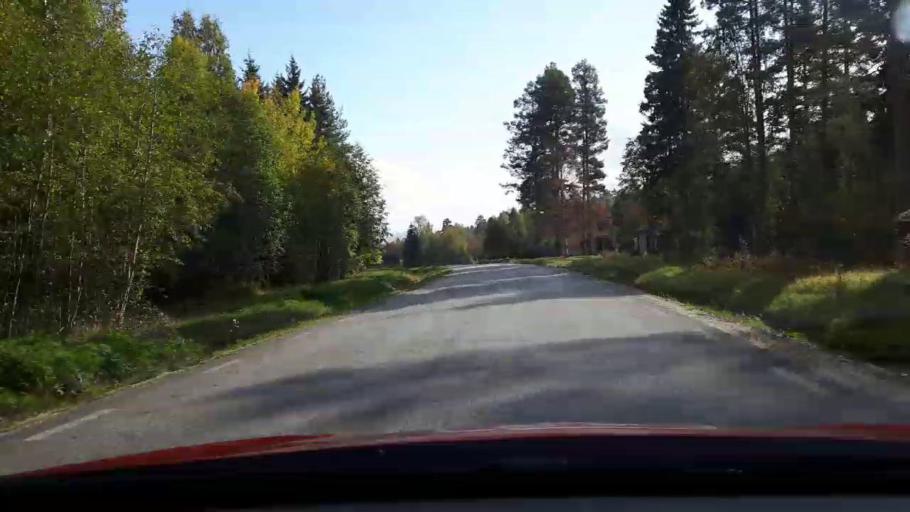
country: SE
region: Gaevleborg
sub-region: Ljusdals Kommun
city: Ljusdal
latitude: 61.7679
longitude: 16.0250
